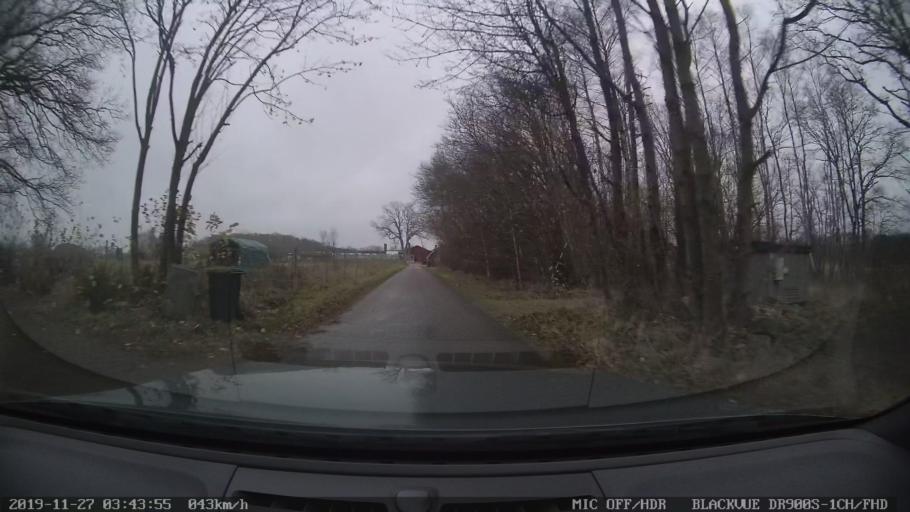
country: SE
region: Skane
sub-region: Hoganas Kommun
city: Hoganas
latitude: 56.2624
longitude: 12.5495
